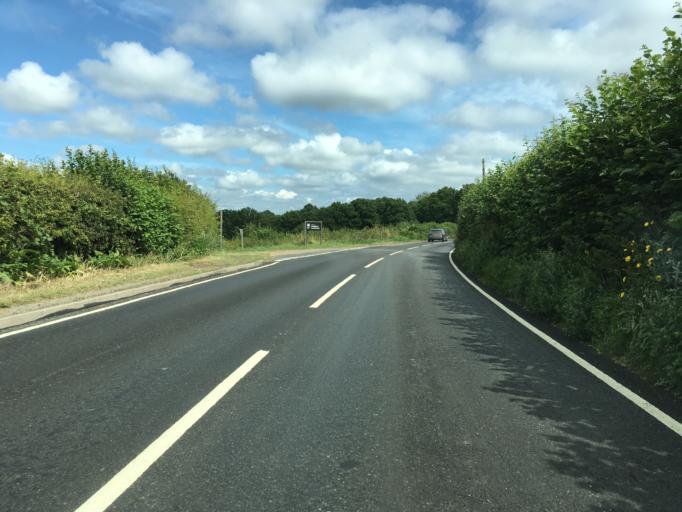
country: GB
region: England
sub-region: Kent
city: Cranbrook
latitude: 51.1101
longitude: 0.5715
